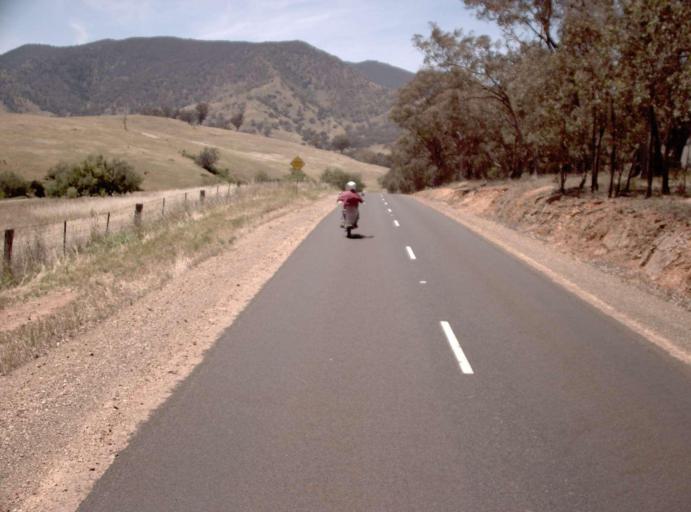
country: AU
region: Victoria
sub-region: East Gippsland
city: Bairnsdale
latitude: -37.1831
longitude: 147.7122
